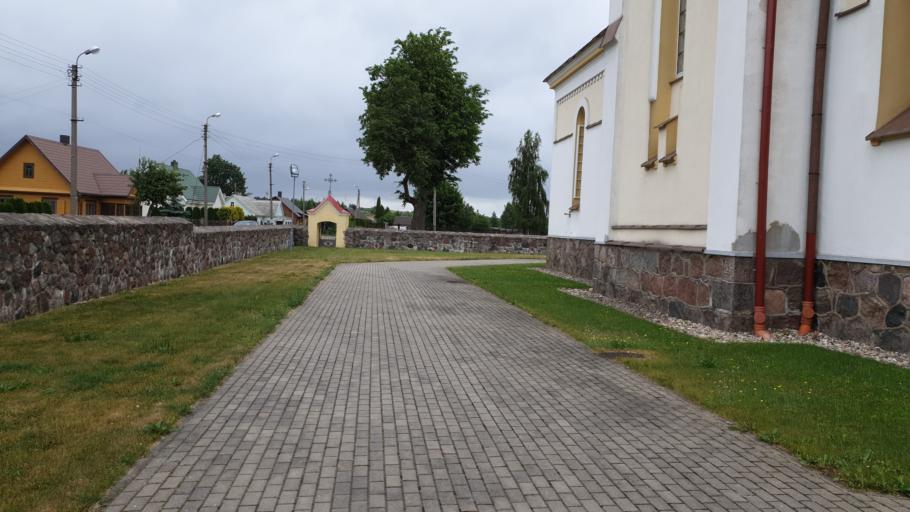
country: LT
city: Svencionys
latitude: 55.1356
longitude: 26.1594
